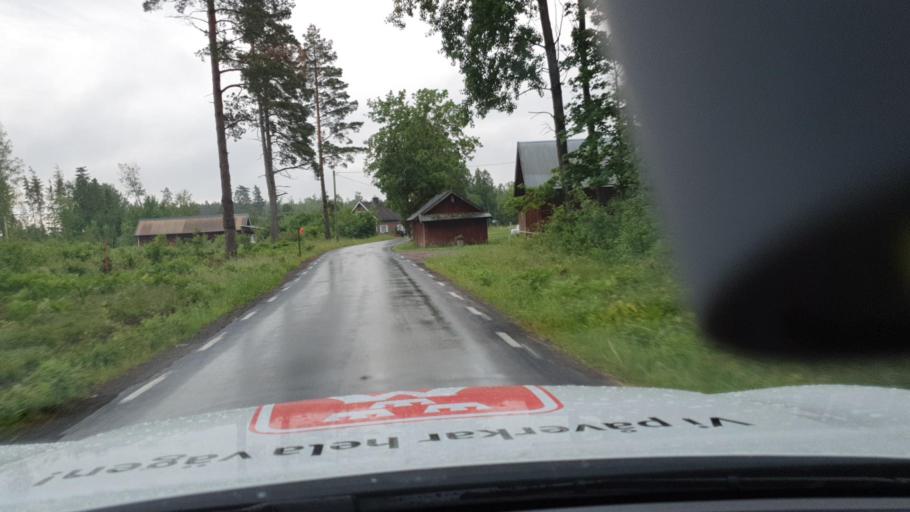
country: SE
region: Vaestra Goetaland
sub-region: Skovde Kommun
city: Stopen
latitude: 58.4482
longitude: 13.9295
